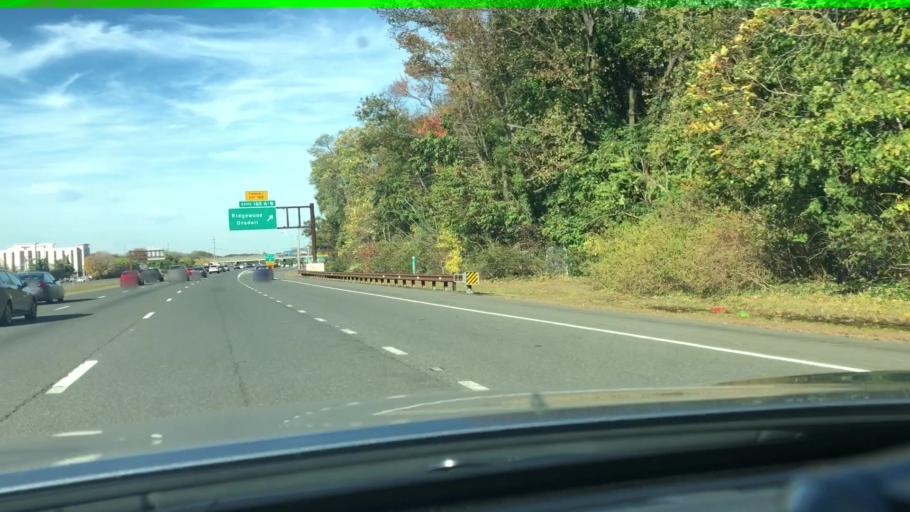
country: US
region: New Jersey
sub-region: Bergen County
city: Paramus
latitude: 40.9569
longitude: -74.0659
